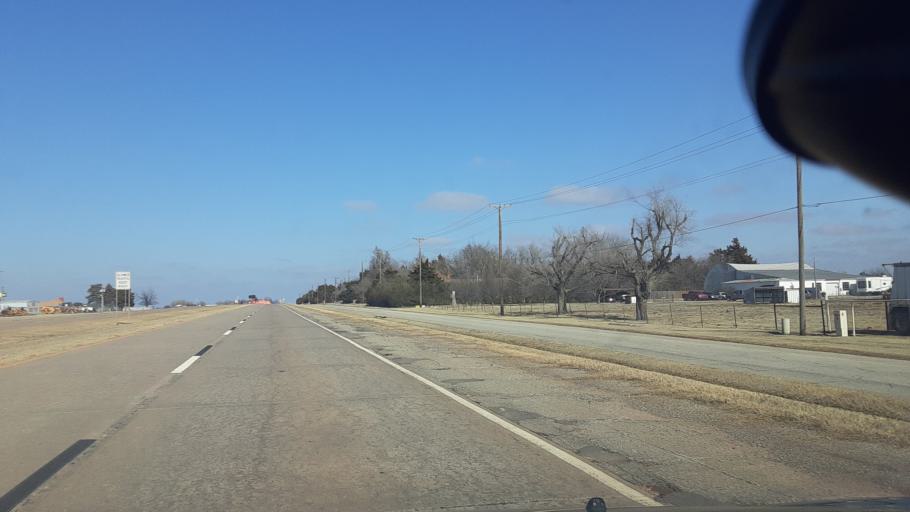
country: US
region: Oklahoma
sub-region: Garfield County
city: Enid
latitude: 36.4533
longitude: -97.8729
